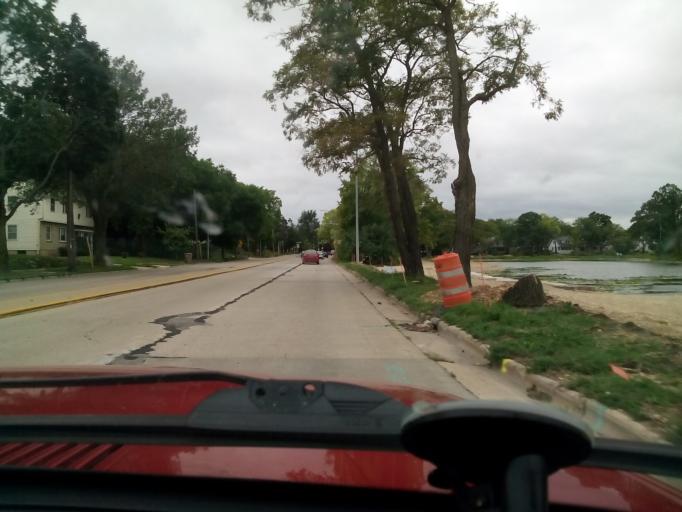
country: US
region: Wisconsin
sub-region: Dane County
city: Maple Bluff
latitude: 43.0916
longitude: -89.3662
